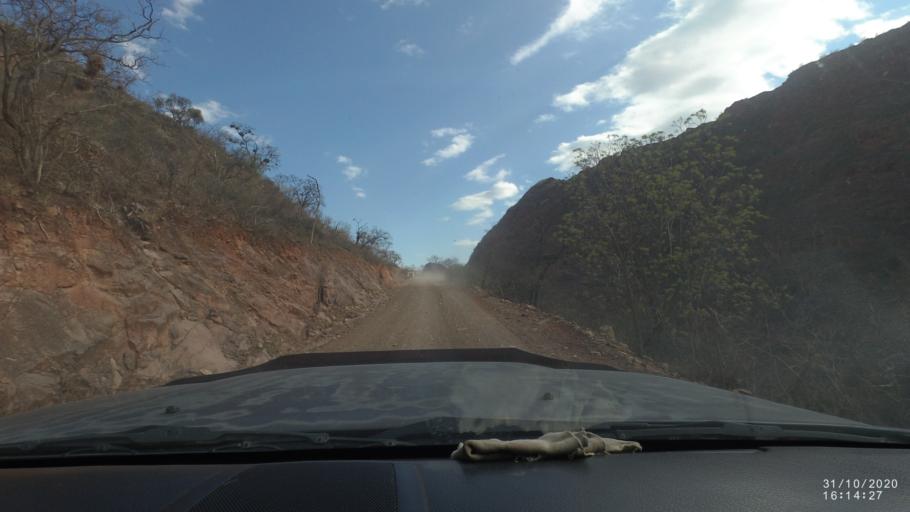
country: BO
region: Chuquisaca
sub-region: Provincia Zudanez
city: Mojocoya
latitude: -18.3836
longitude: -64.6148
